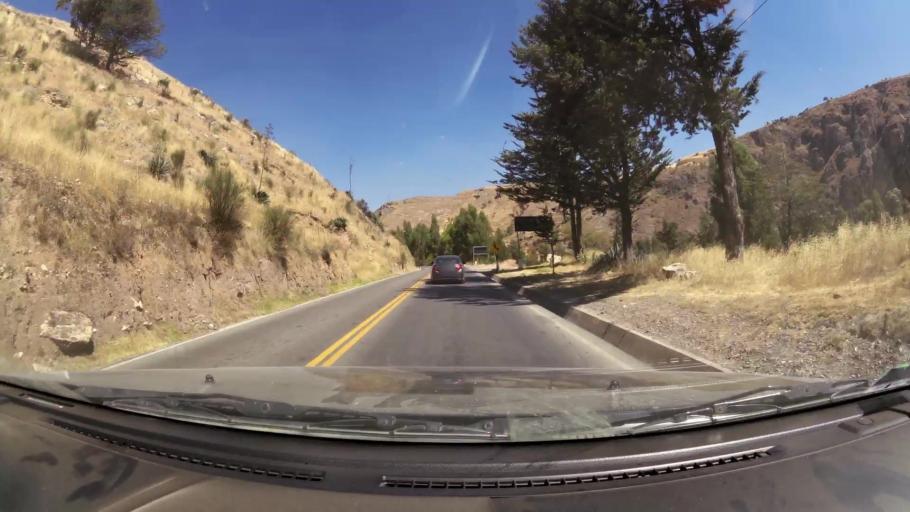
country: PE
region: Junin
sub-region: Provincia de Jauja
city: Sausa
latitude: -11.8065
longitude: -75.4916
